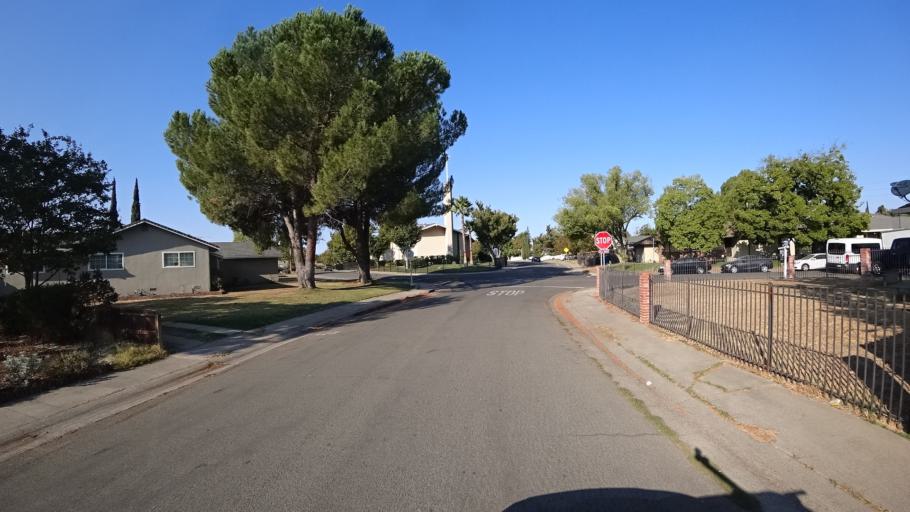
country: US
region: California
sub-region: Sacramento County
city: Parkway
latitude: 38.4946
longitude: -121.4955
